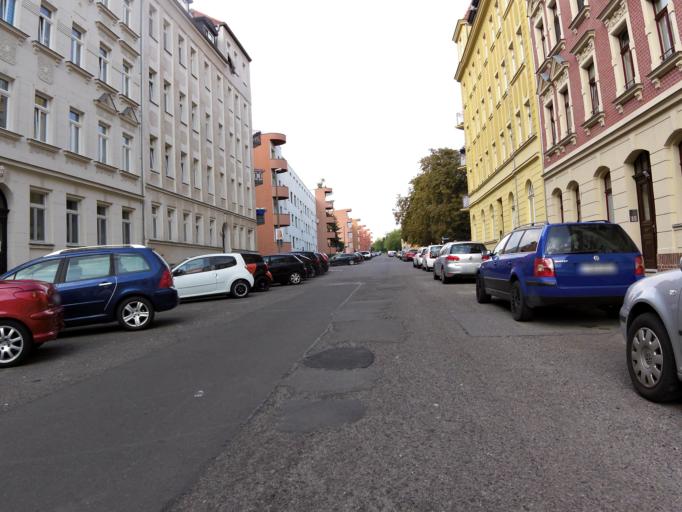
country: DE
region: Saxony
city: Leipzig
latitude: 51.3676
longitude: 12.3484
